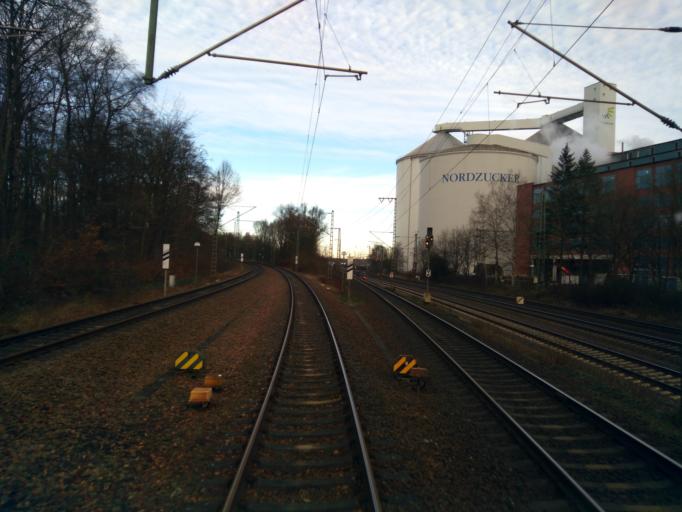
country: DE
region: Lower Saxony
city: Uelzen
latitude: 52.9758
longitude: 10.5557
